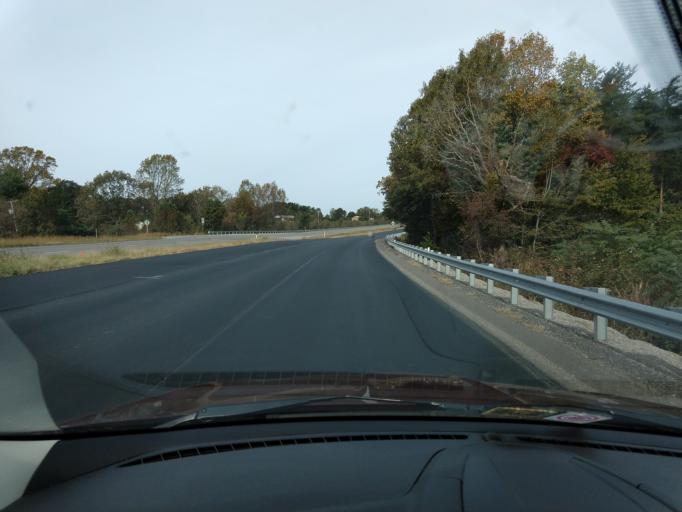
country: US
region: Virginia
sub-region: Pittsylvania County
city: Chatham
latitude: 36.8682
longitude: -79.4068
